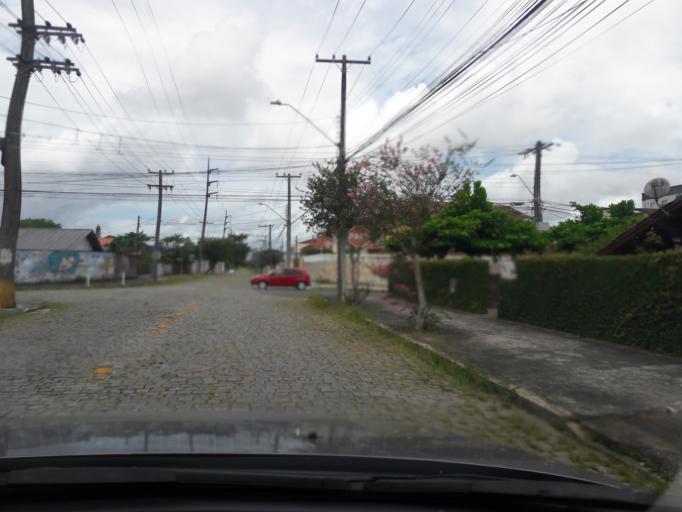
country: BR
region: Santa Catarina
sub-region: Joinville
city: Joinville
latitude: -26.3188
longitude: -48.8396
